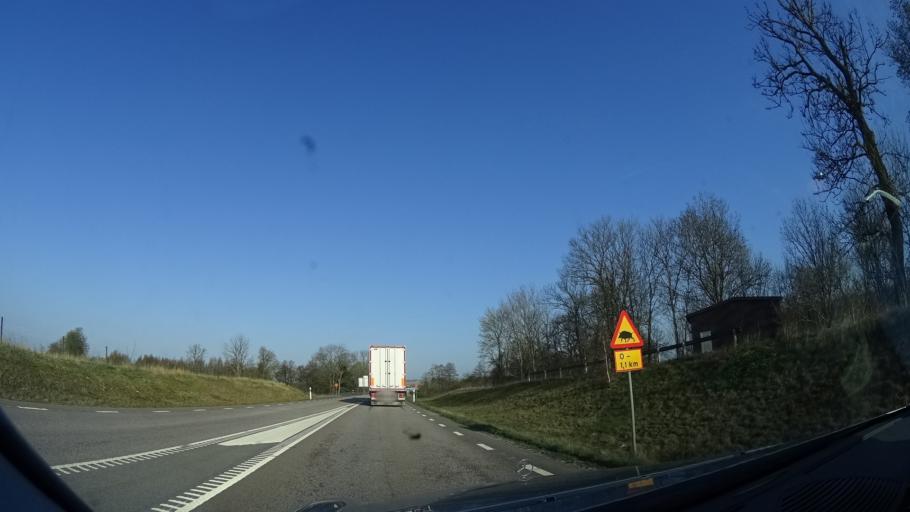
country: SE
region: Skane
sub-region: Eslovs Kommun
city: Eslov
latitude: 55.8624
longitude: 13.2380
